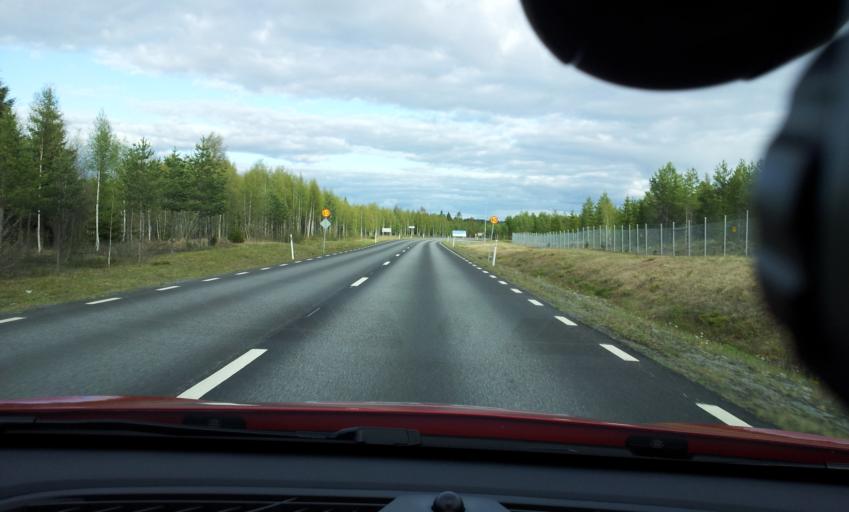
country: SE
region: Jaemtland
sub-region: Krokoms Kommun
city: Krokom
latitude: 63.2019
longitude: 14.4926
